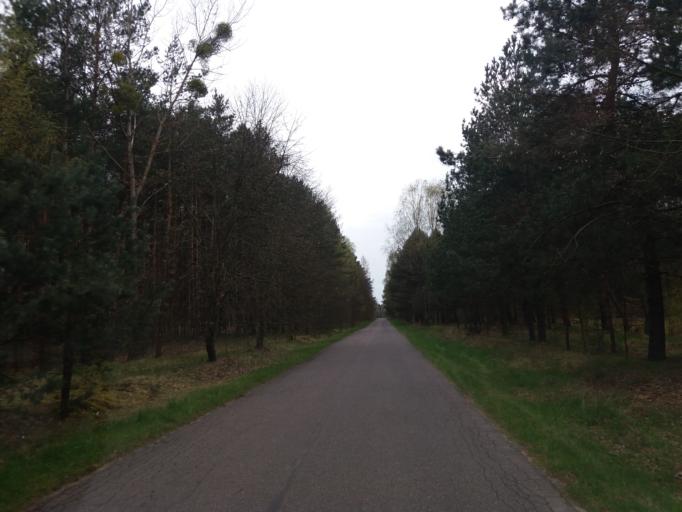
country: PL
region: West Pomeranian Voivodeship
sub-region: Powiat choszczenski
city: Bierzwnik
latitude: 53.0437
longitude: 15.6387
